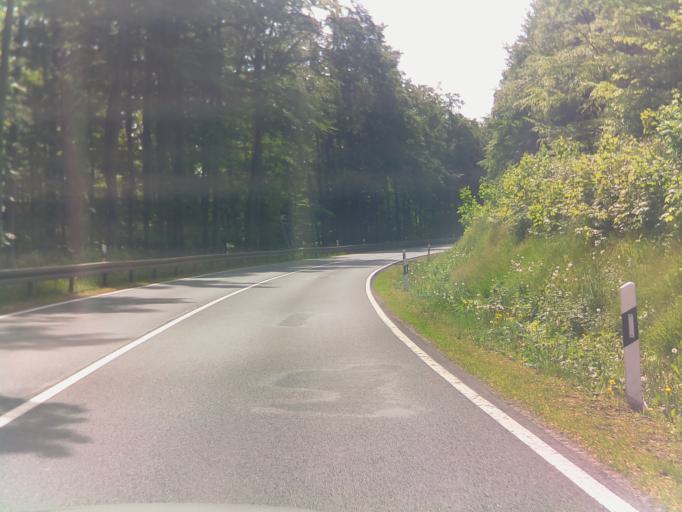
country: DE
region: Saxony-Anhalt
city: Blankenburg
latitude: 51.7557
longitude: 10.9551
